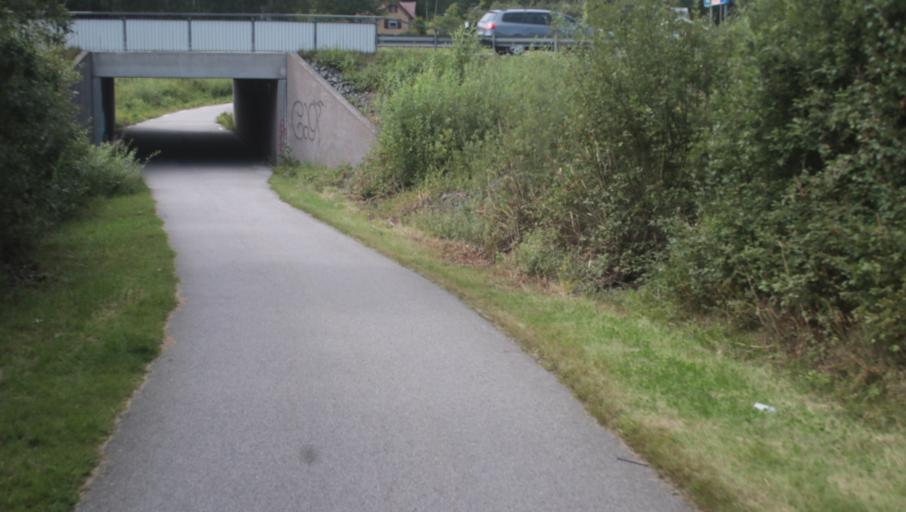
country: SE
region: Blekinge
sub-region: Karlshamns Kommun
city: Karlshamn
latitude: 56.2014
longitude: 14.8123
